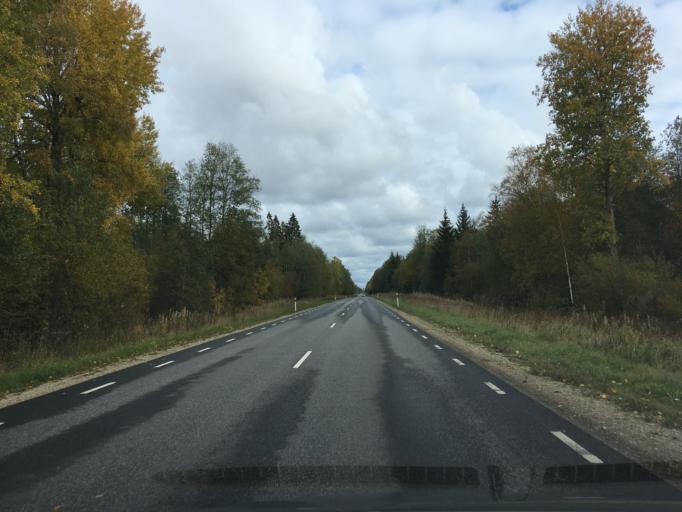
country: EE
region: Harju
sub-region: Anija vald
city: Kehra
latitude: 59.2282
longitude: 25.2767
